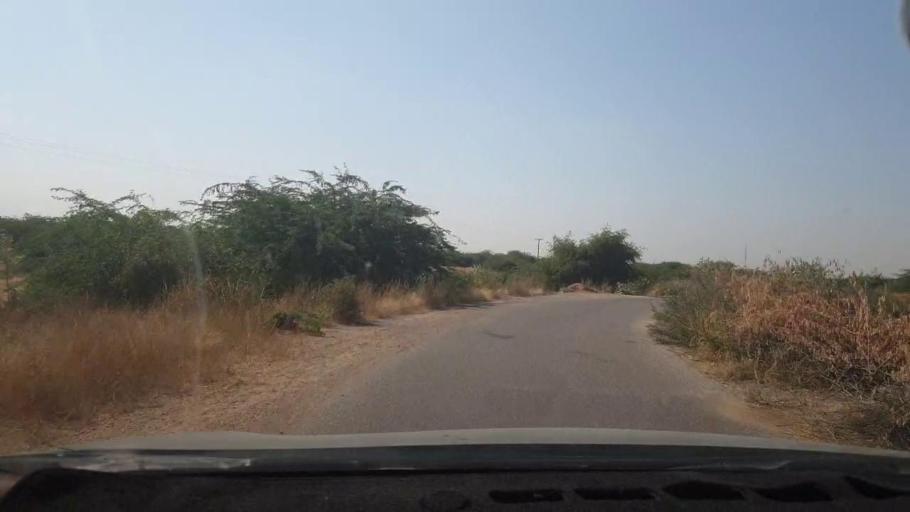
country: PK
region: Sindh
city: Malir Cantonment
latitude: 25.1566
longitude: 67.1402
